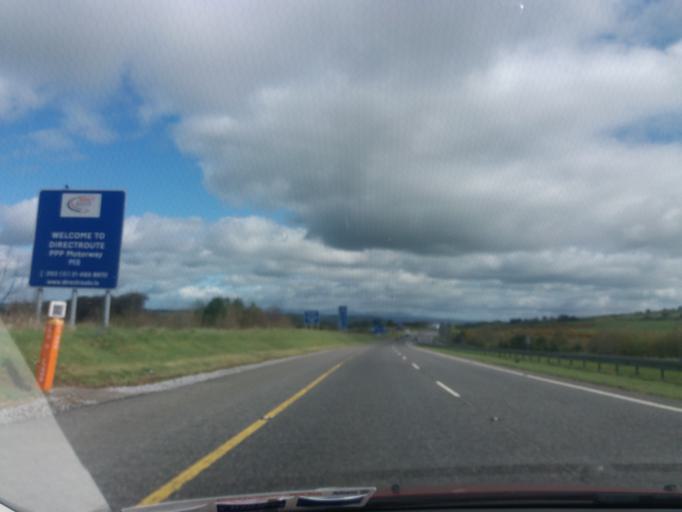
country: IE
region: Munster
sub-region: County Cork
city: Watergrasshill
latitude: 52.0192
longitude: -8.3350
